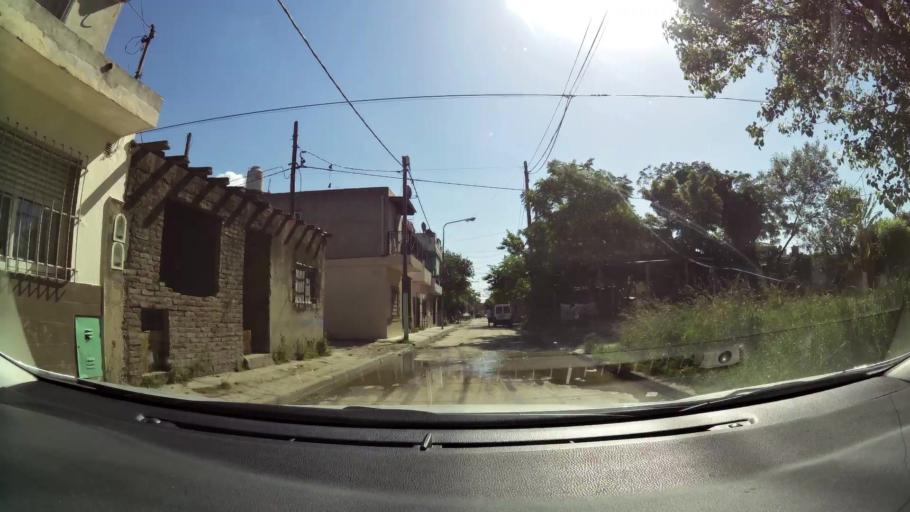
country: AR
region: Buenos Aires F.D.
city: Villa Lugano
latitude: -34.7089
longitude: -58.4782
